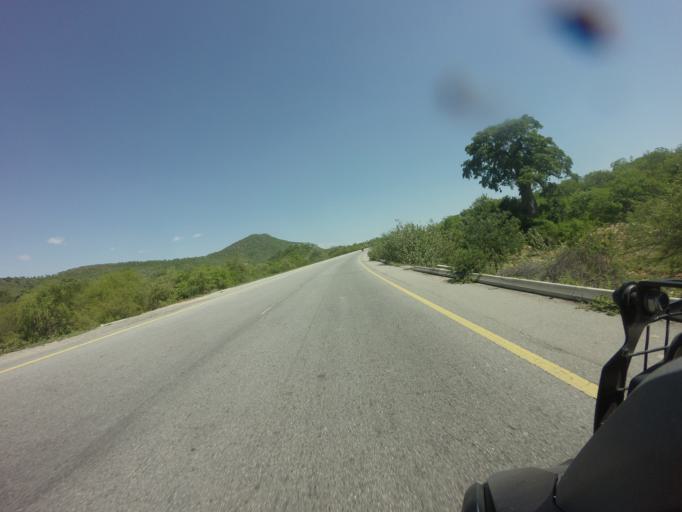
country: AO
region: Benguela
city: Benguela
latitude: -13.2725
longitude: 13.7981
